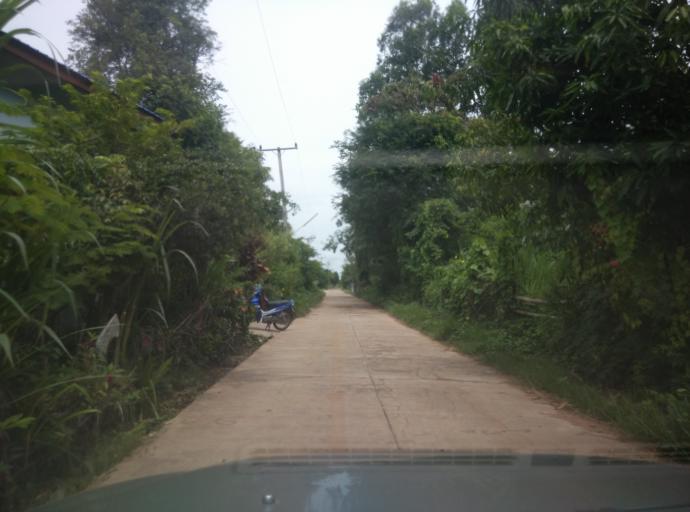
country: TH
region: Sisaket
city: Huai Thap Than
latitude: 15.0467
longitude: 104.0803
